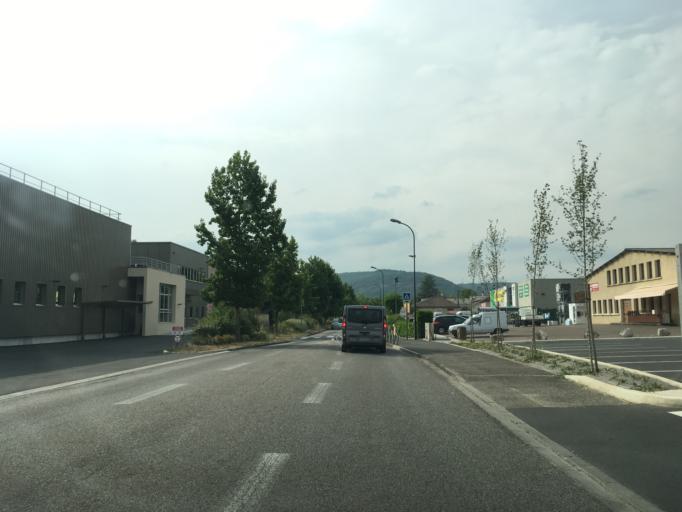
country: FR
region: Midi-Pyrenees
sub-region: Departement du Lot
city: Souillac
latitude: 44.8944
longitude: 1.4691
